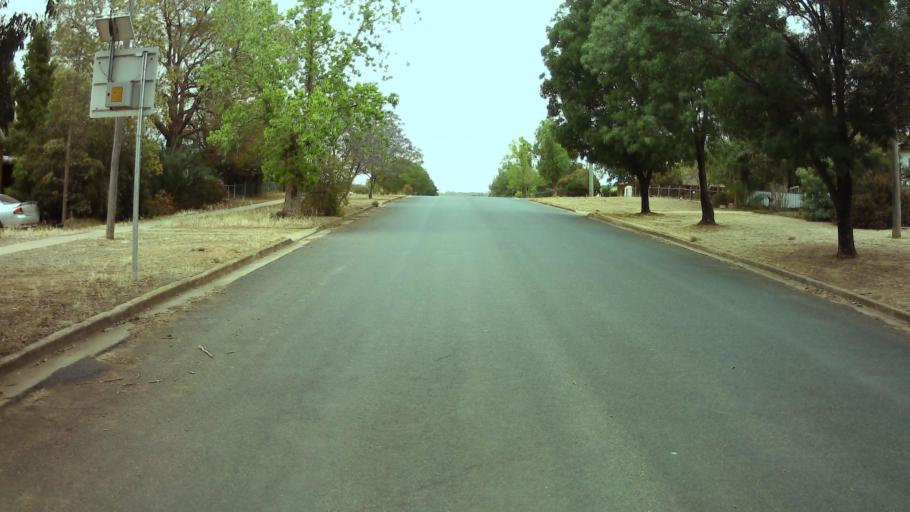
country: AU
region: New South Wales
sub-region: Weddin
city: Grenfell
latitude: -33.9013
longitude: 148.1645
